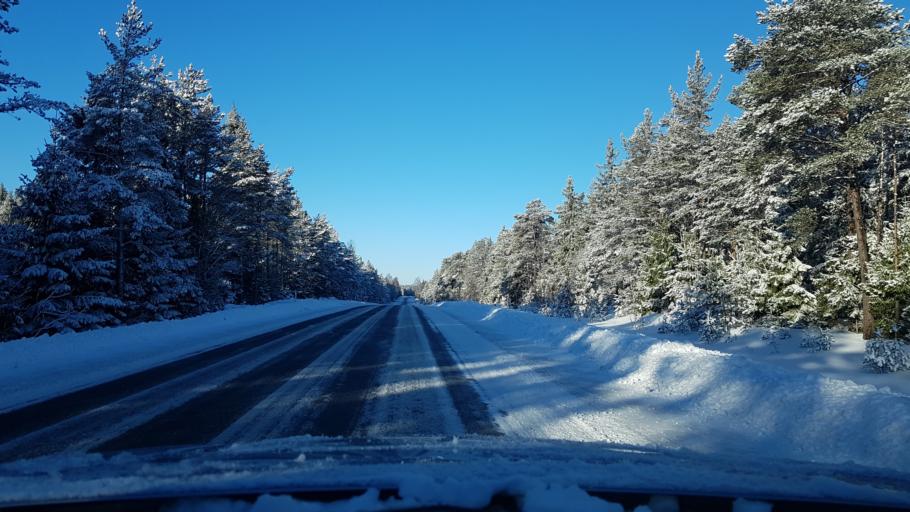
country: EE
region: Hiiumaa
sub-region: Kaerdla linn
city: Kardla
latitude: 58.9599
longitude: 22.8528
